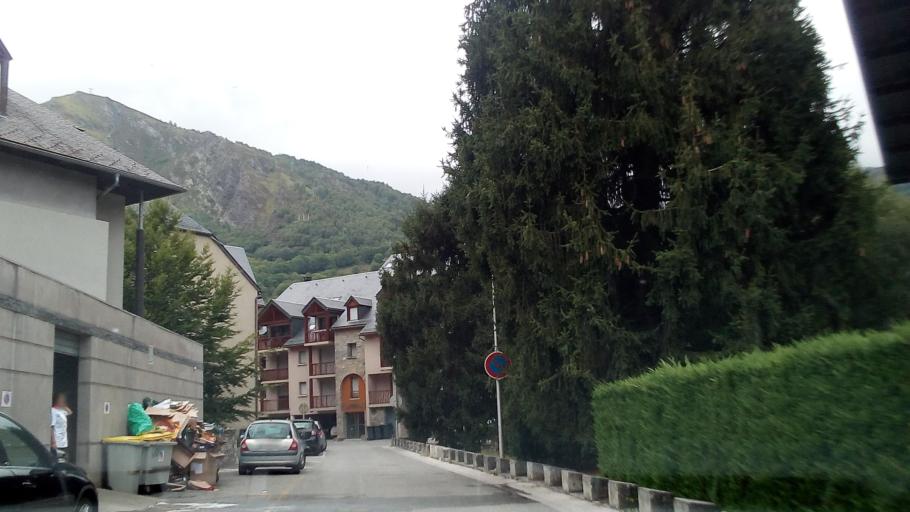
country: FR
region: Midi-Pyrenees
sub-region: Departement des Hautes-Pyrenees
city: Saint-Lary-Soulan
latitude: 42.8178
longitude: 0.3255
